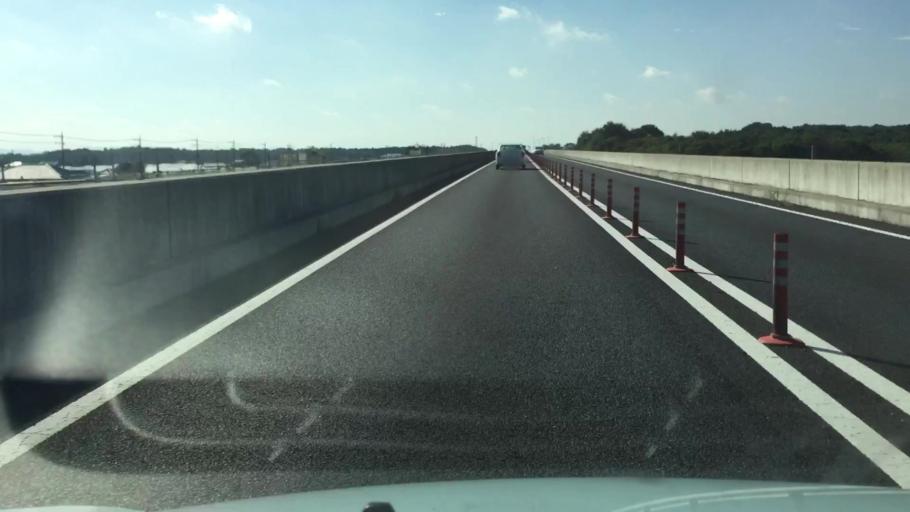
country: JP
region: Tochigi
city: Mooka
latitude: 36.5123
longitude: 139.9867
